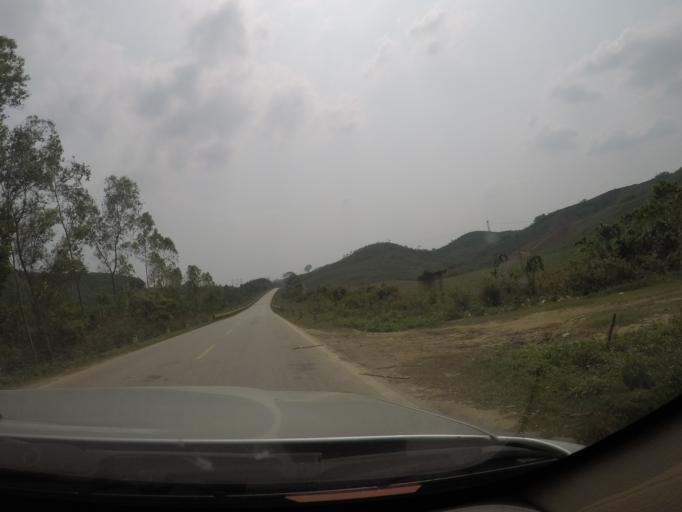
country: VN
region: Thanh Hoa
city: Thi Tran Yen Cat
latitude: 19.5176
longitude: 105.3976
